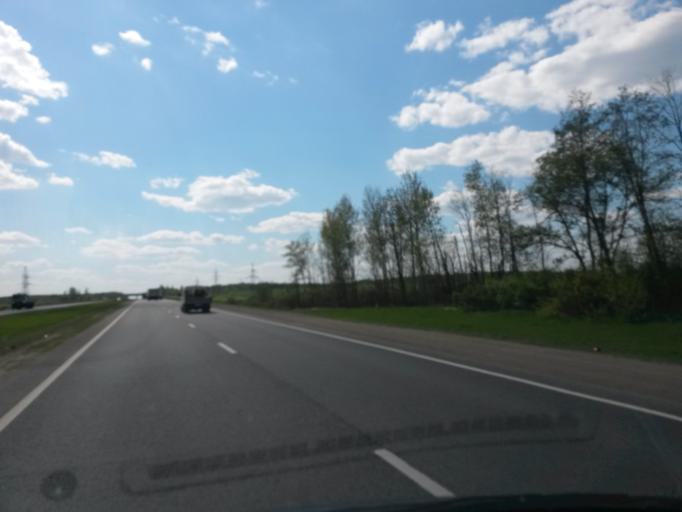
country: RU
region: Jaroslavl
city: Krasnyye Tkachi
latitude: 57.4432
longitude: 39.7152
